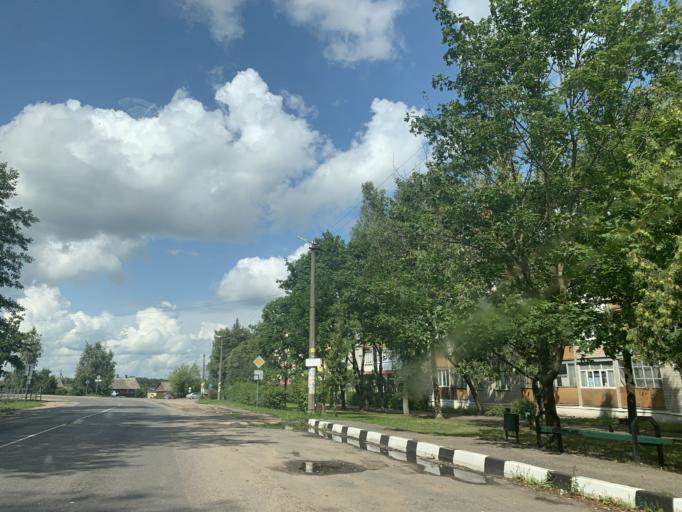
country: BY
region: Minsk
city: Enyerhyetykaw
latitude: 53.5866
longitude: 27.0527
